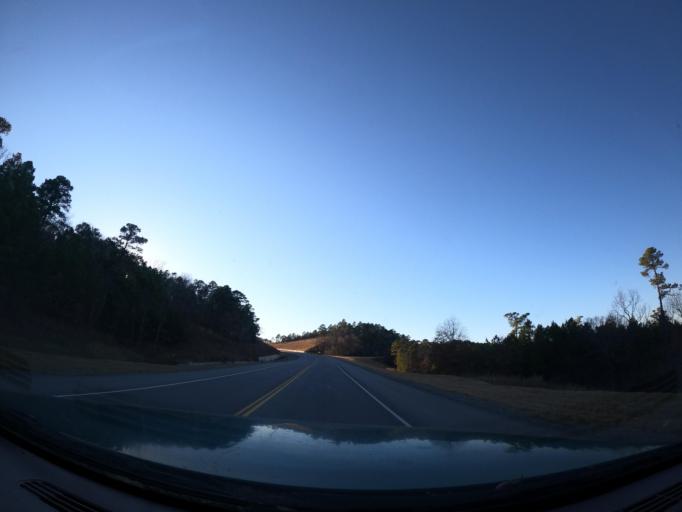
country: US
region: Oklahoma
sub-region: Pittsburg County
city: Hartshorne
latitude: 34.8913
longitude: -95.4530
